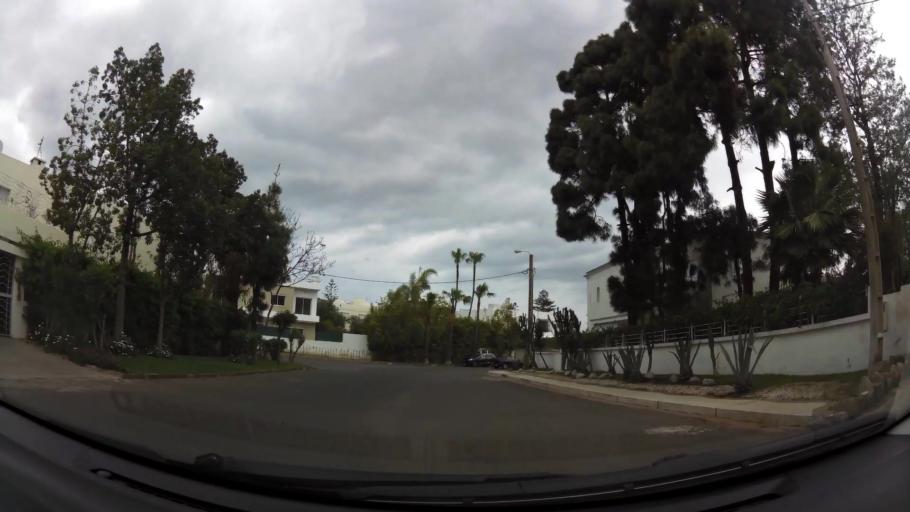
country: MA
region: Grand Casablanca
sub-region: Casablanca
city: Casablanca
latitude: 33.5789
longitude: -7.6602
